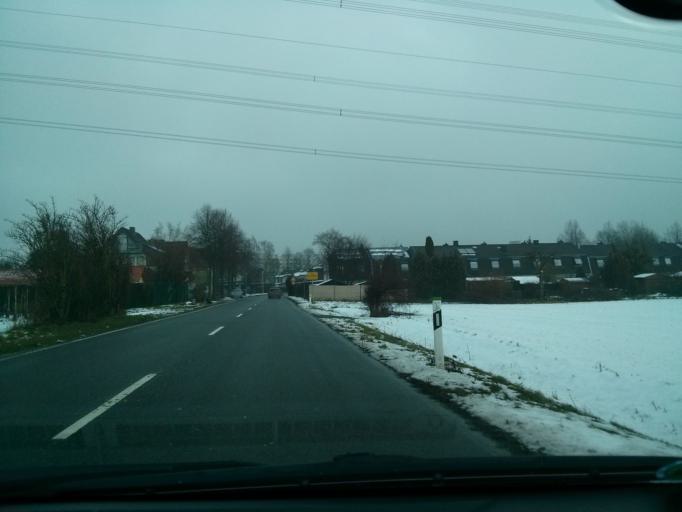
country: DE
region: North Rhine-Westphalia
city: Meckenheim
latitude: 50.6162
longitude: 7.0235
